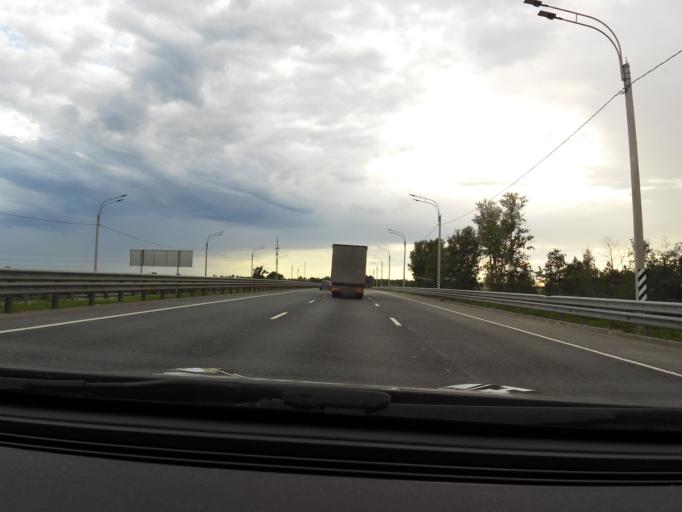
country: RU
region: Vladimir
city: Vorsha
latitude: 56.0669
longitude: 40.1462
